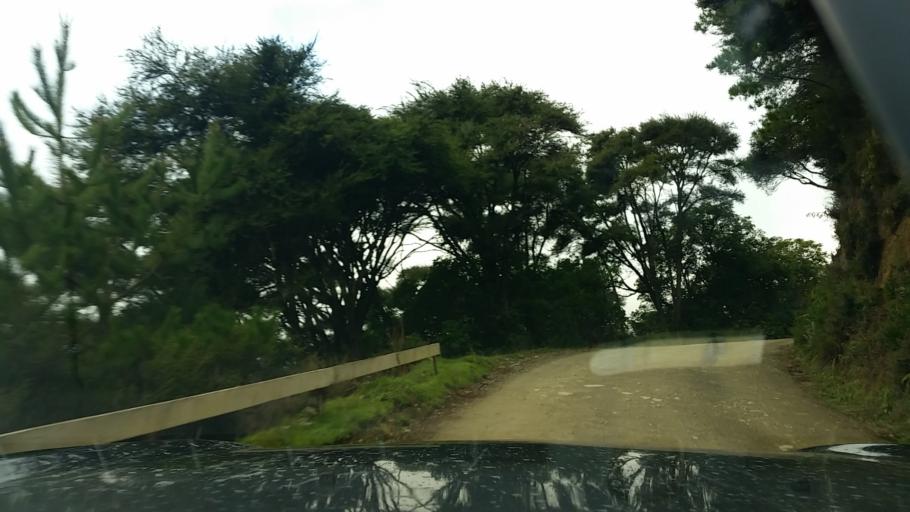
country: NZ
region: Marlborough
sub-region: Marlborough District
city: Picton
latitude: -41.1771
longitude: 174.0568
